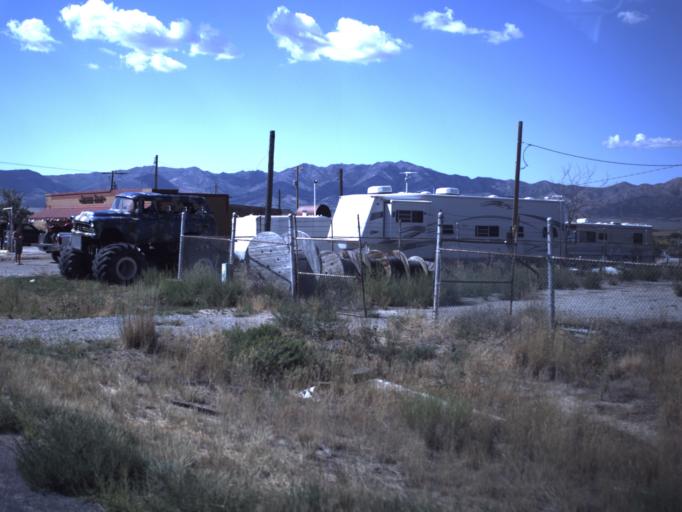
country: US
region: Utah
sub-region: Tooele County
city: Tooele
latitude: 40.0932
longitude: -112.4309
